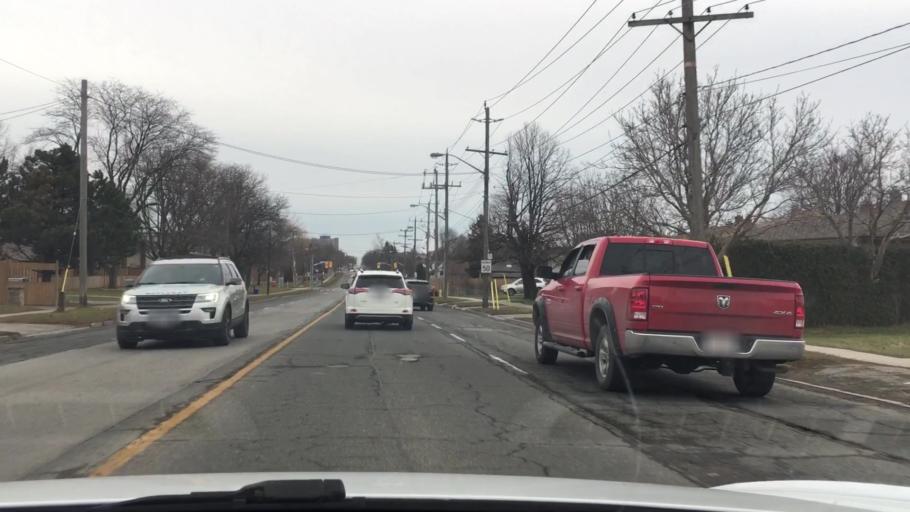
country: CA
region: Ontario
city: Scarborough
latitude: 43.7481
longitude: -79.2638
